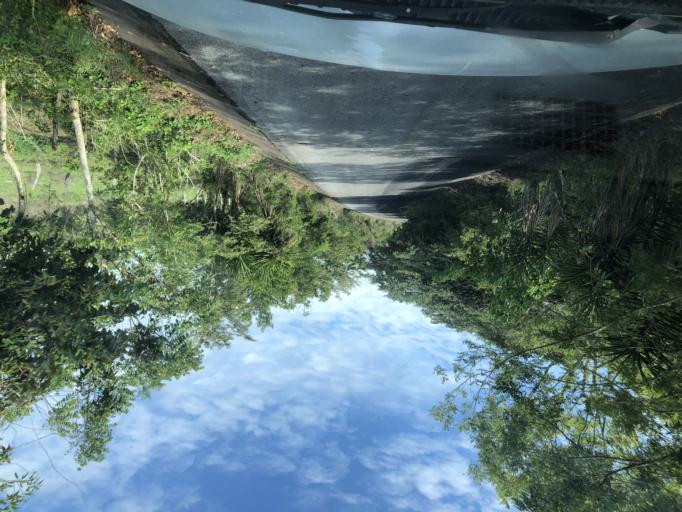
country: MX
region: Veracruz
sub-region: Alto Lucero de Gutierrez Barrios
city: Palma Sola
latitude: 19.7998
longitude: -96.5456
